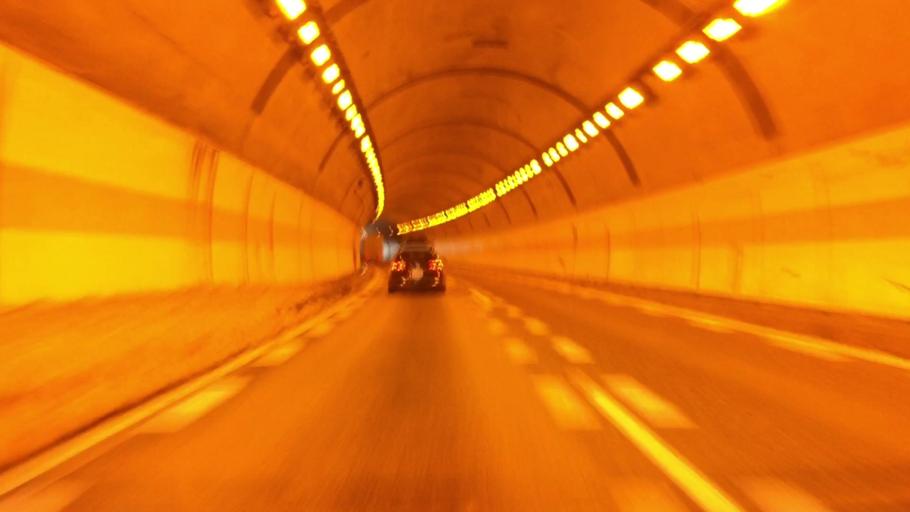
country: JP
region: Gunma
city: Numata
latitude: 36.7554
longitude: 138.9670
